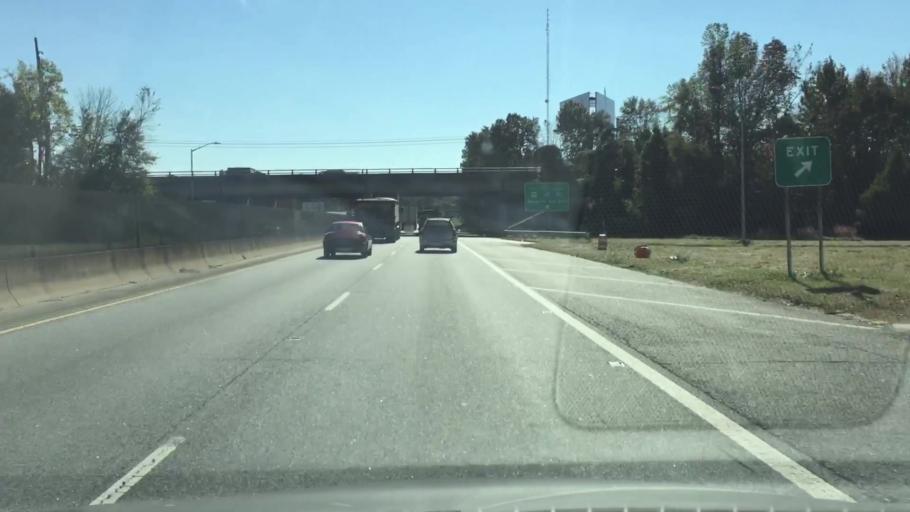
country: US
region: North Carolina
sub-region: Guilford County
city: Greensboro
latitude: 36.0885
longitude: -79.7663
